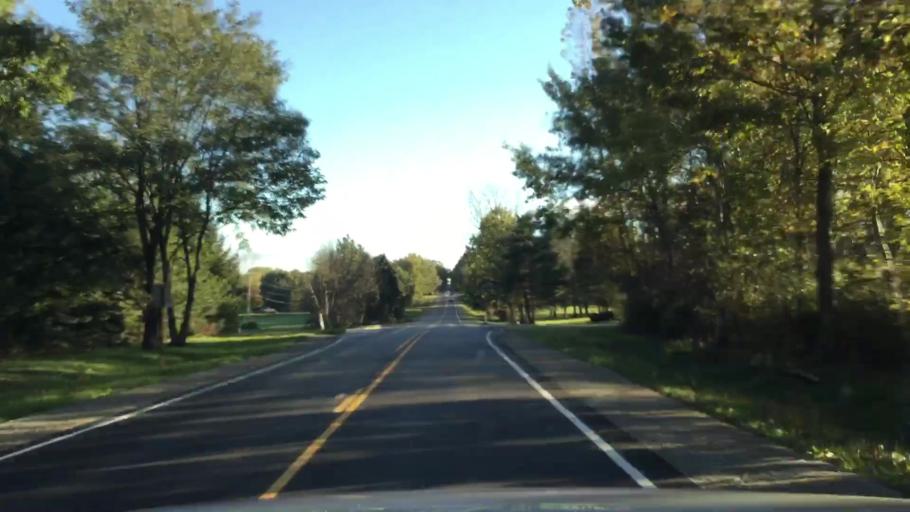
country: US
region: Michigan
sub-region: Lapeer County
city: Almont
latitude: 42.9246
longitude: -83.1437
